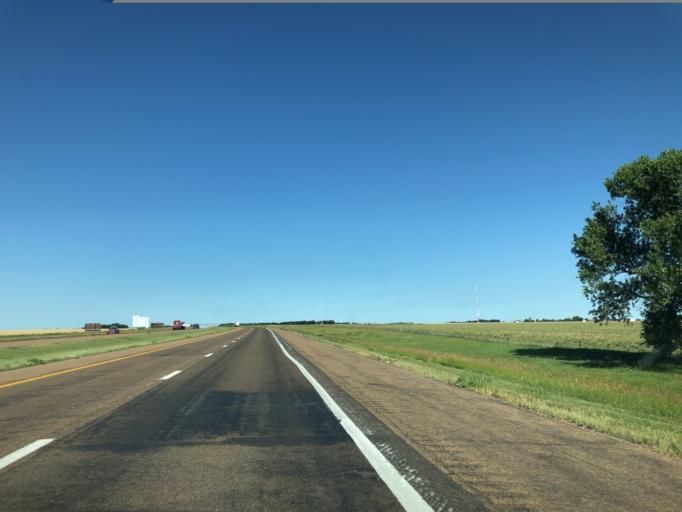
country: US
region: Kansas
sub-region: Sherman County
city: Goodland
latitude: 39.3292
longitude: -101.7447
